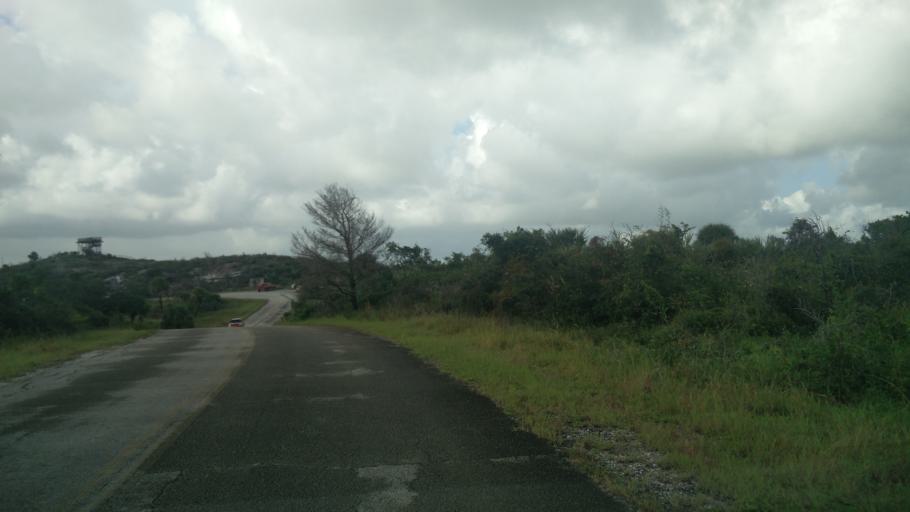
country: US
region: Florida
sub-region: Palm Beach County
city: Tequesta
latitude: 27.0153
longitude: -80.1097
